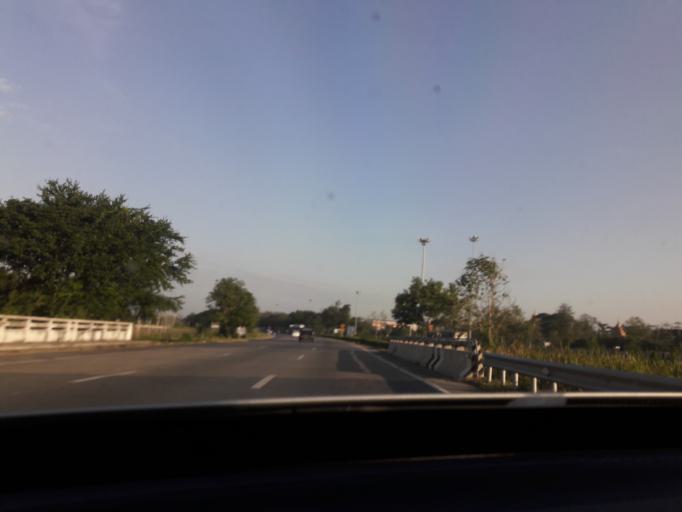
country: TH
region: Phra Nakhon Si Ayutthaya
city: Bang Pahan
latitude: 14.4619
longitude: 100.5378
